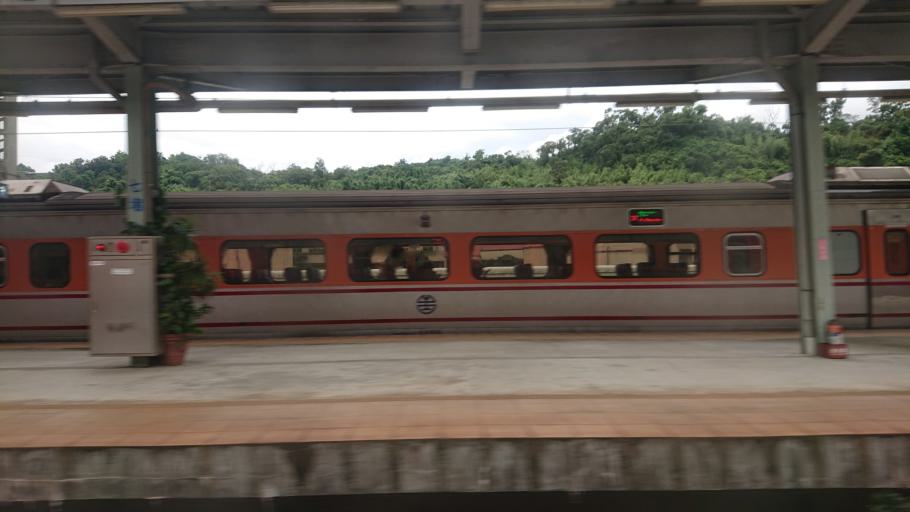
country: TW
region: Taiwan
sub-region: Keelung
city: Keelung
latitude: 25.0923
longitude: 121.7131
